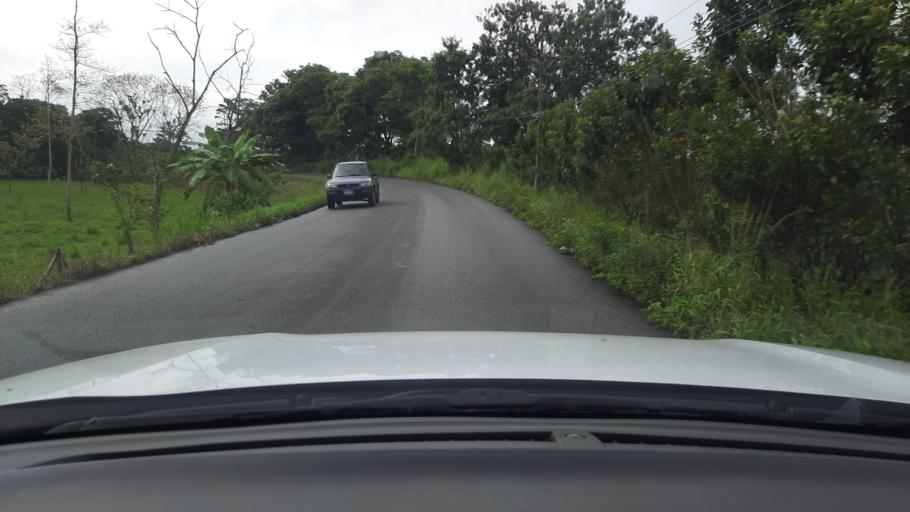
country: CR
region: Alajuela
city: San Jose
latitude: 10.9283
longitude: -85.0960
